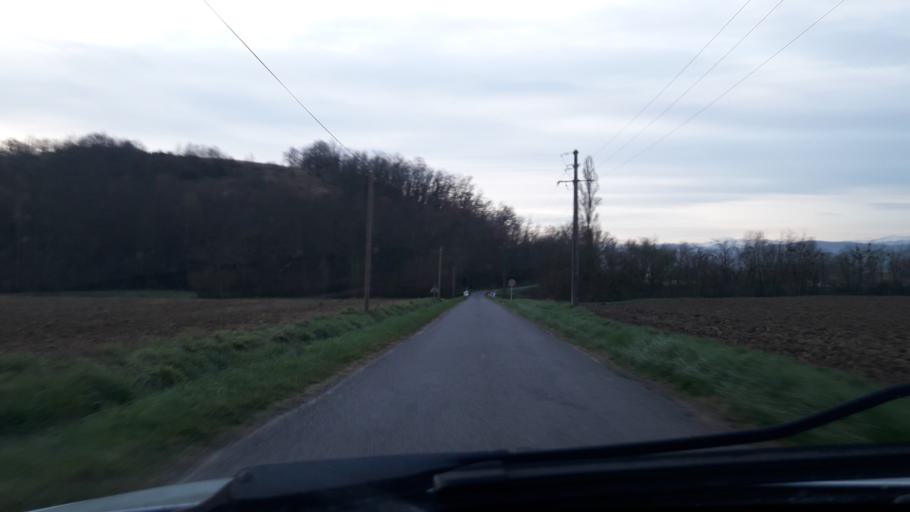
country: FR
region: Midi-Pyrenees
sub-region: Departement de la Haute-Garonne
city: Montesquieu-Volvestre
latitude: 43.1916
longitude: 1.2527
